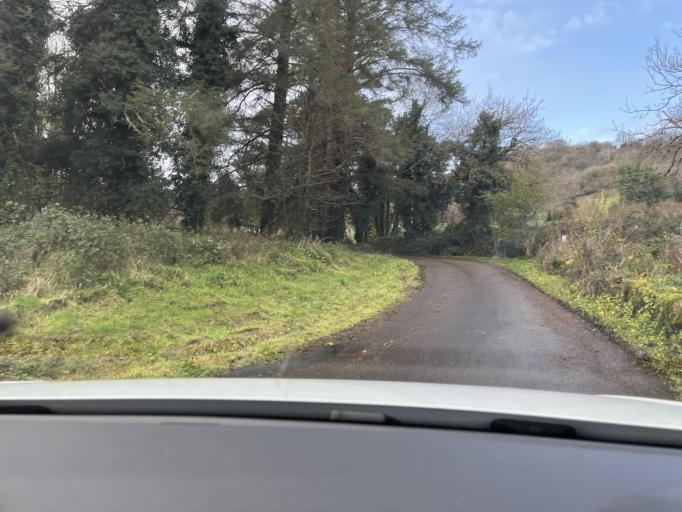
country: IE
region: Connaught
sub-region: Sligo
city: Sligo
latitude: 54.2675
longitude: -8.3468
